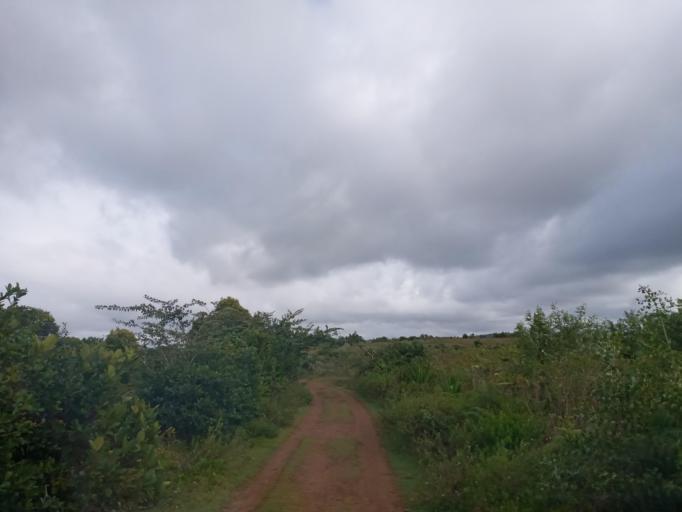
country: MG
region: Atsimo-Atsinanana
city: Vohipaho
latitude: -23.7797
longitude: 47.5408
